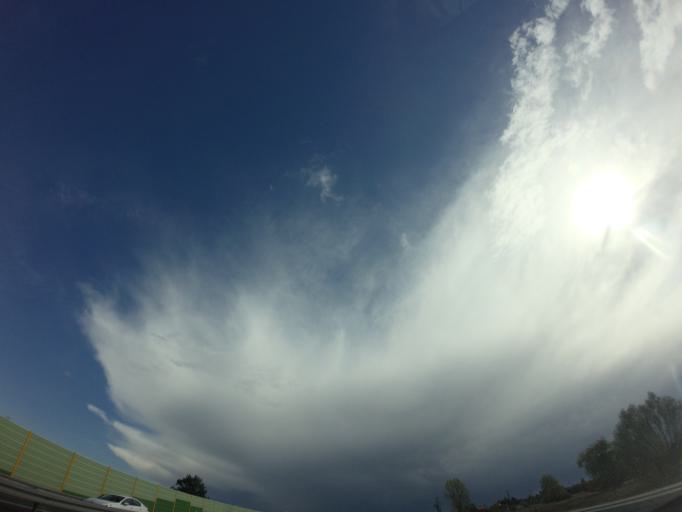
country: PL
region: Lubusz
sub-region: Powiat gorzowski
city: Deszczno
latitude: 52.6895
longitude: 15.2789
